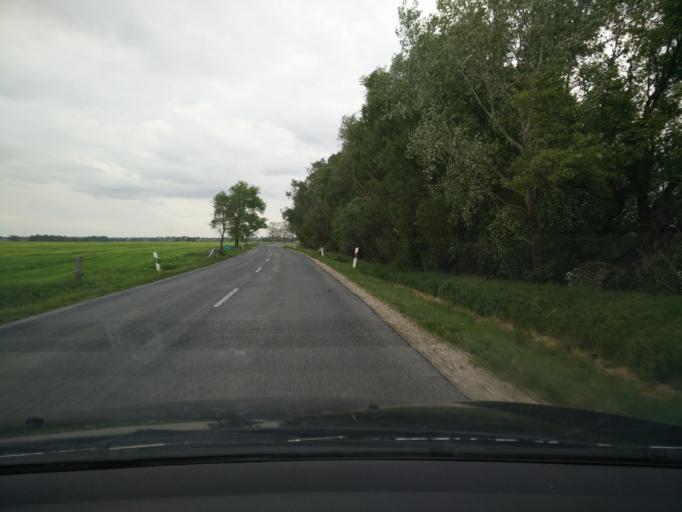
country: HU
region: Gyor-Moson-Sopron
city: Tet
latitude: 47.4969
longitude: 17.5033
